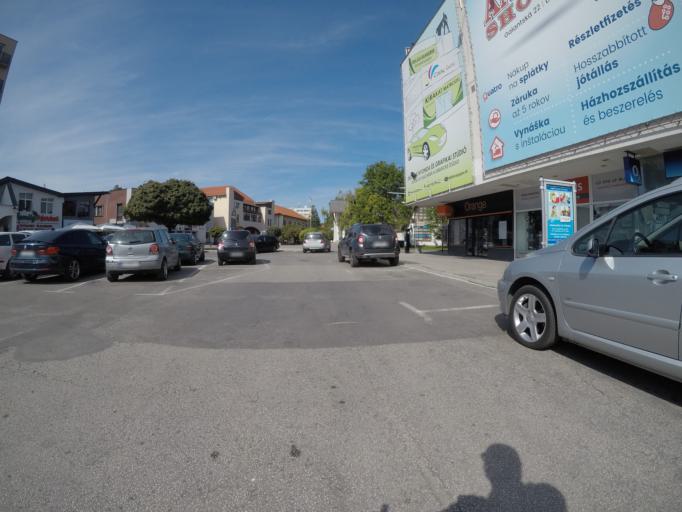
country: SK
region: Trnavsky
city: Dunajska Streda
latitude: 47.9930
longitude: 17.6169
